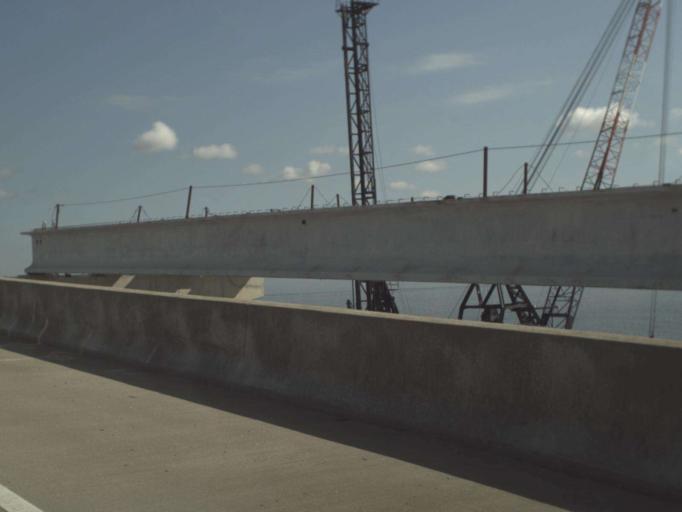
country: US
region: Florida
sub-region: Walton County
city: Seaside
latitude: 30.3978
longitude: -86.1699
